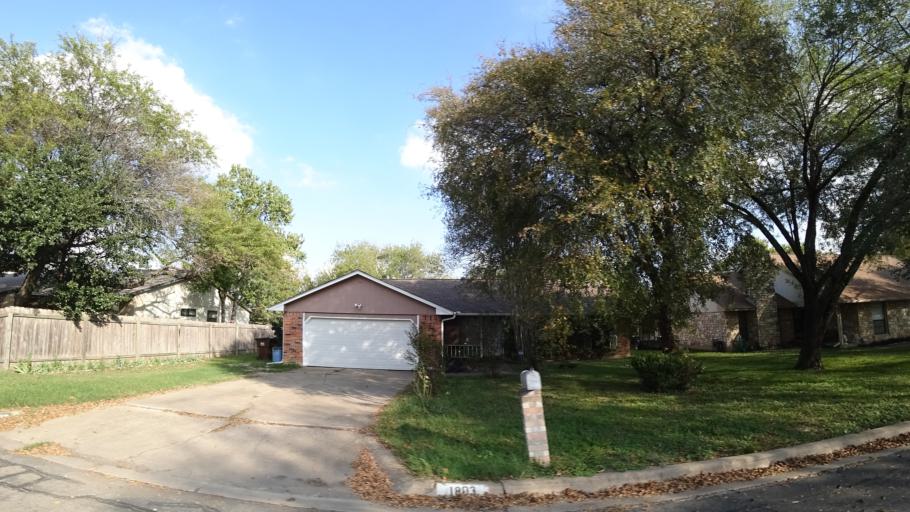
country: US
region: Texas
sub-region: Williamson County
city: Round Rock
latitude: 30.4940
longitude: -97.6676
